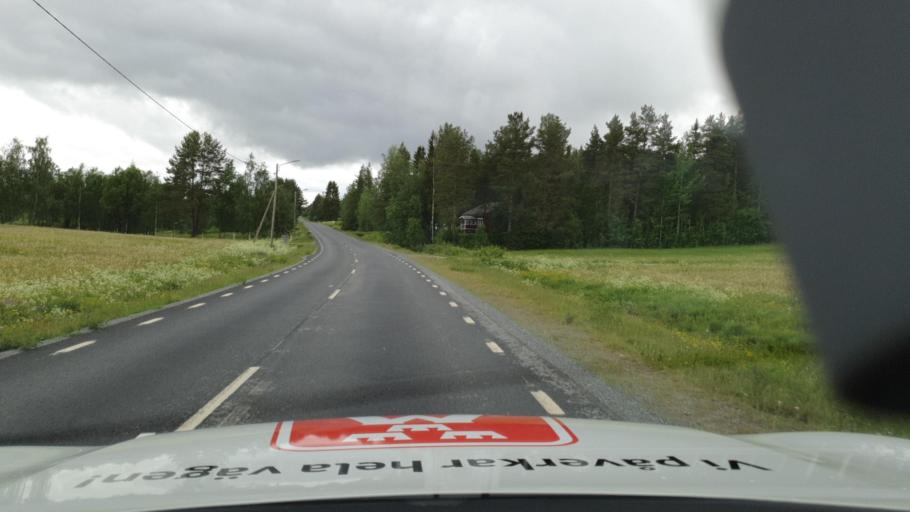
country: SE
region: Vaesterbotten
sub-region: Dorotea Kommun
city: Dorotea
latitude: 64.2213
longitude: 16.5450
